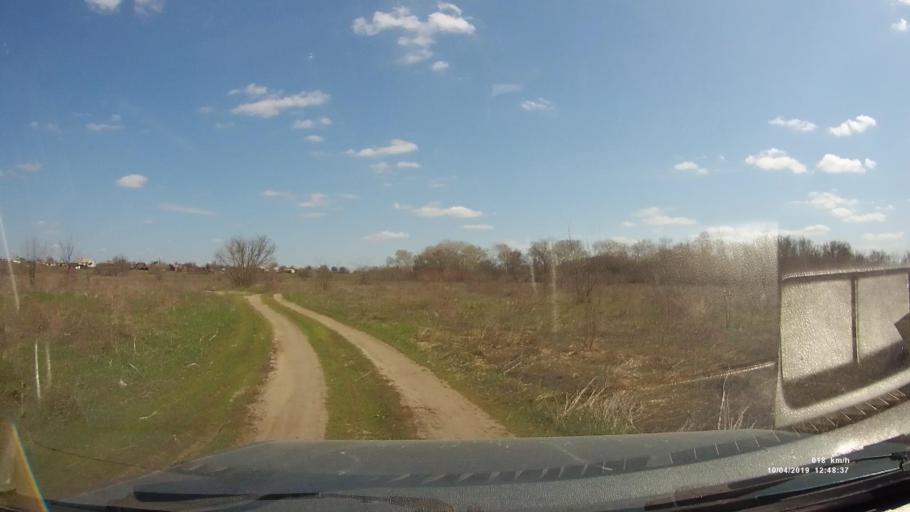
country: RU
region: Rostov
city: Kamensk-Shakhtinskiy
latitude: 48.3558
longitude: 40.2233
